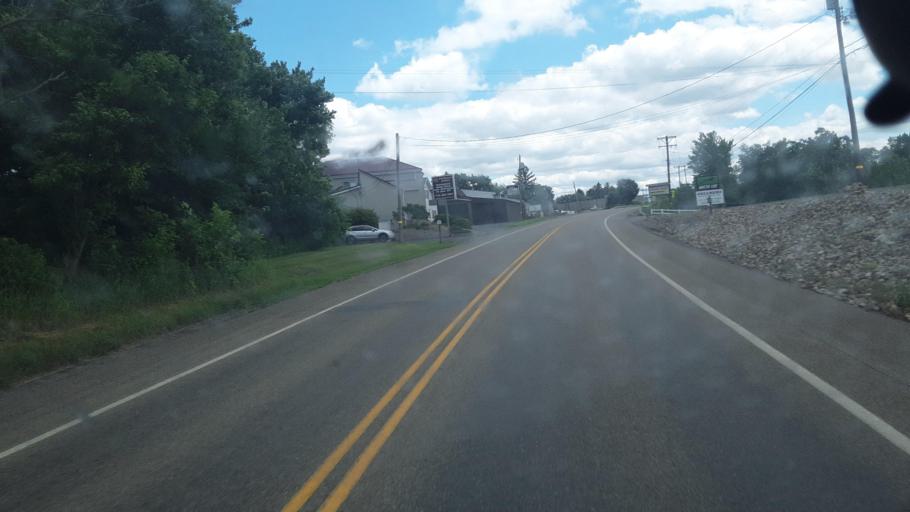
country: US
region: Pennsylvania
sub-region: Butler County
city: Prospect
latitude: 40.9339
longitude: -80.1469
